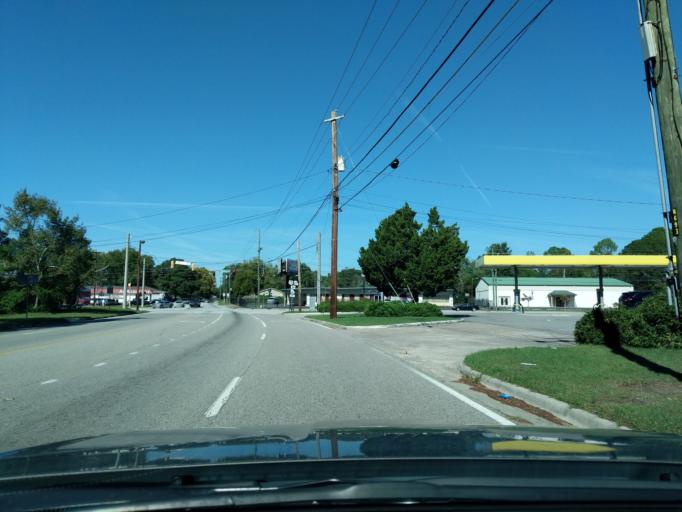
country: US
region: Georgia
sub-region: Richmond County
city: Augusta
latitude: 33.4345
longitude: -82.0093
